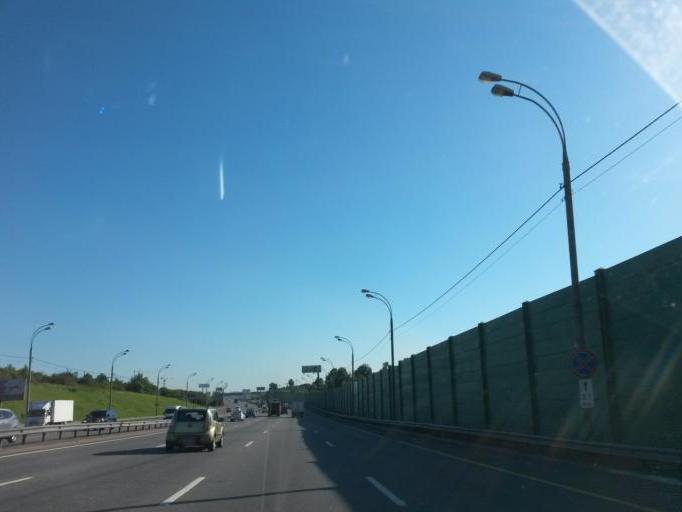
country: RU
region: Moskovskaya
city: Vidnoye
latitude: 55.5558
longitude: 37.6845
